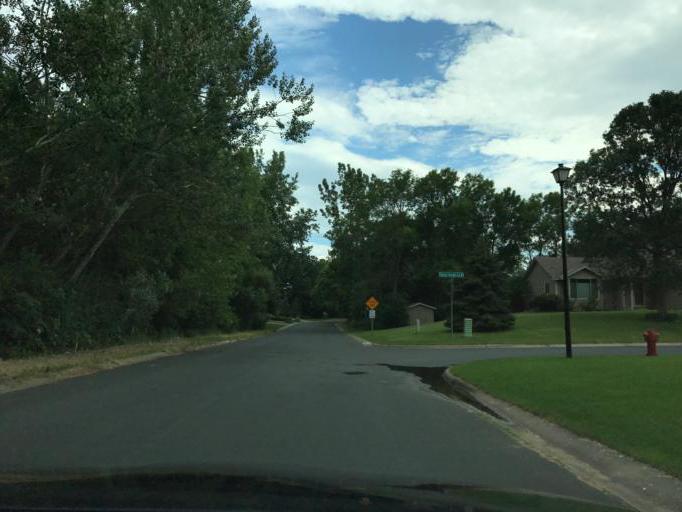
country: US
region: Minnesota
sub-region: Hennepin County
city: Osseo
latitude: 45.0827
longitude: -93.4134
